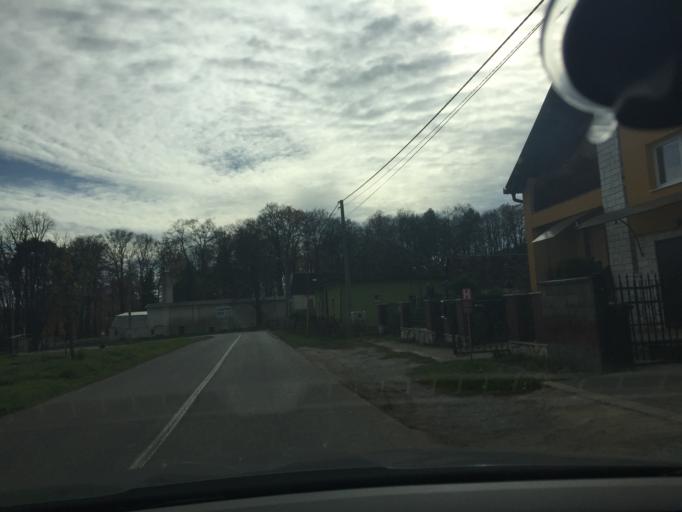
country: SK
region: Presovsky
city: Spisske Podhradie
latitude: 48.9908
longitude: 20.7809
